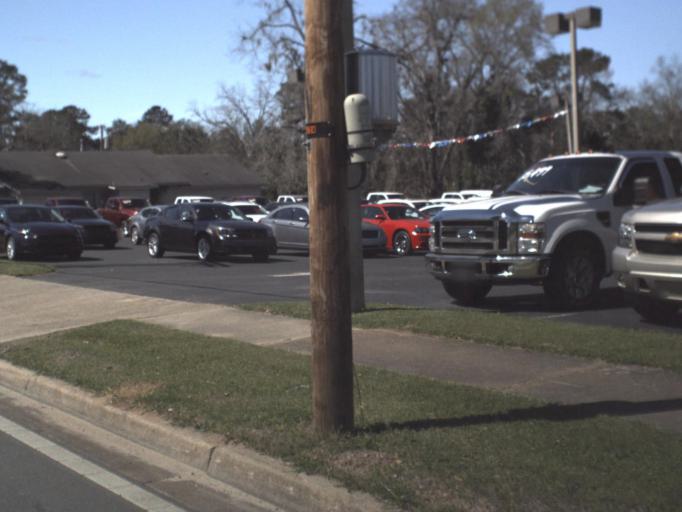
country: US
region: Florida
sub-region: Gadsden County
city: Quincy
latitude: 30.5856
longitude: -84.5993
